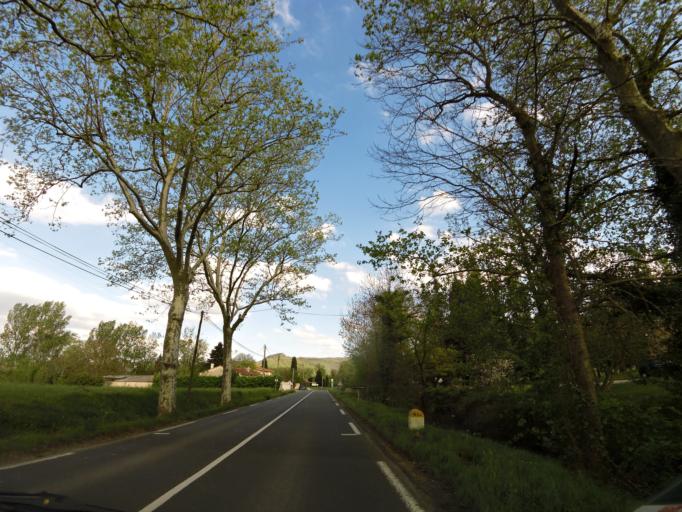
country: FR
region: Midi-Pyrenees
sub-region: Departement de la Haute-Garonne
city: Revel
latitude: 43.4529
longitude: 2.0357
